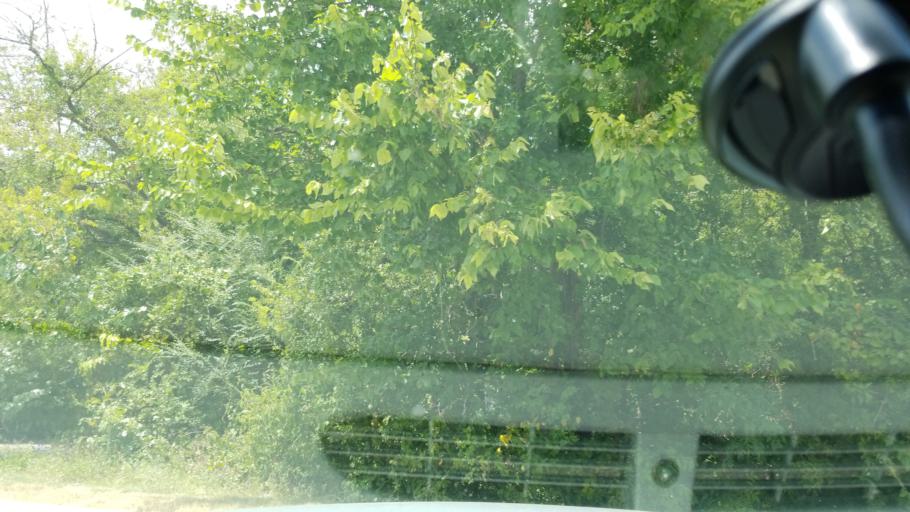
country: US
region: Texas
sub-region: Dallas County
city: Grand Prairie
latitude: 32.7544
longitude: -96.9982
